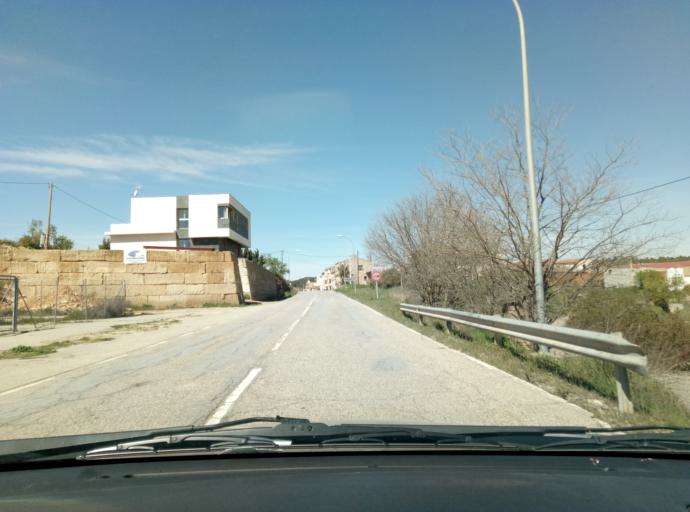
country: ES
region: Catalonia
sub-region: Provincia de Lleida
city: Vinaixa
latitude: 41.4275
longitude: 0.9801
